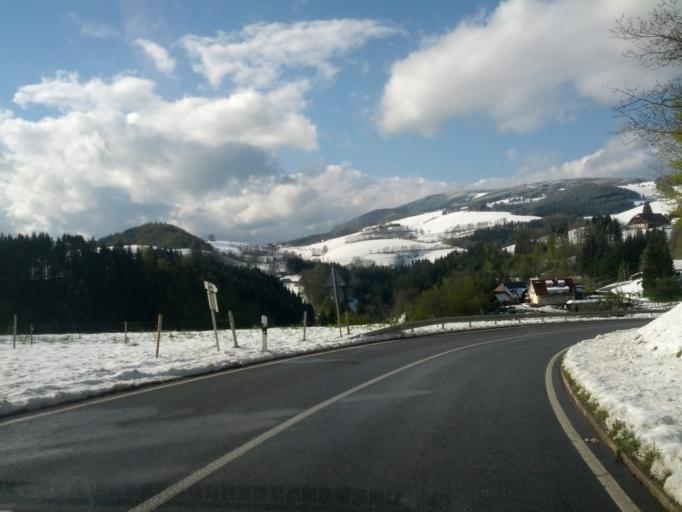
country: DE
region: Baden-Wuerttemberg
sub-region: Freiburg Region
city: Sankt Peter
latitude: 48.0225
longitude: 8.0298
